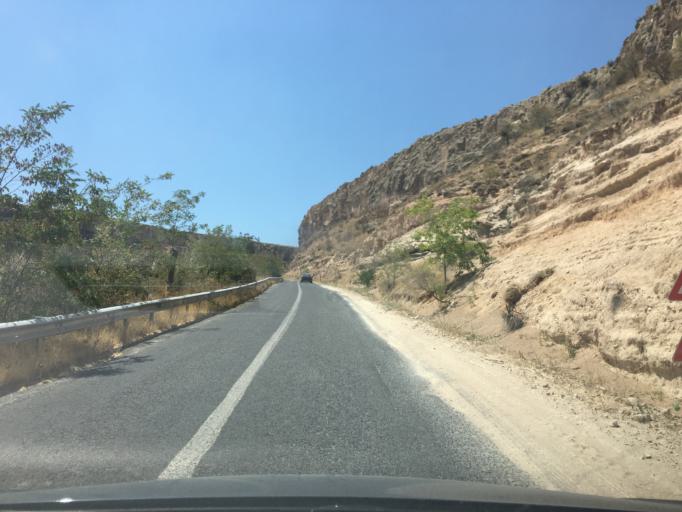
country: TR
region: Nevsehir
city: Urgub
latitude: 38.4675
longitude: 34.9384
